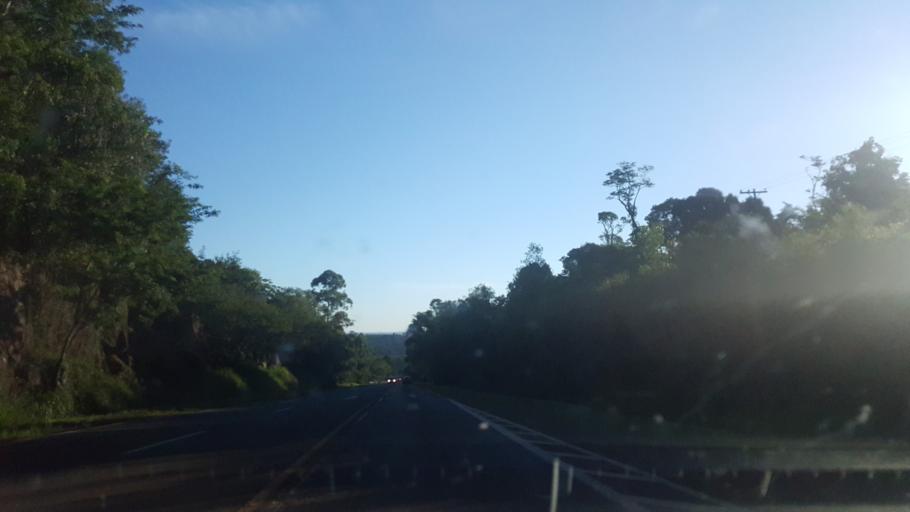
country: AR
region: Misiones
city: El Alcazar
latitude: -26.7271
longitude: -54.8683
